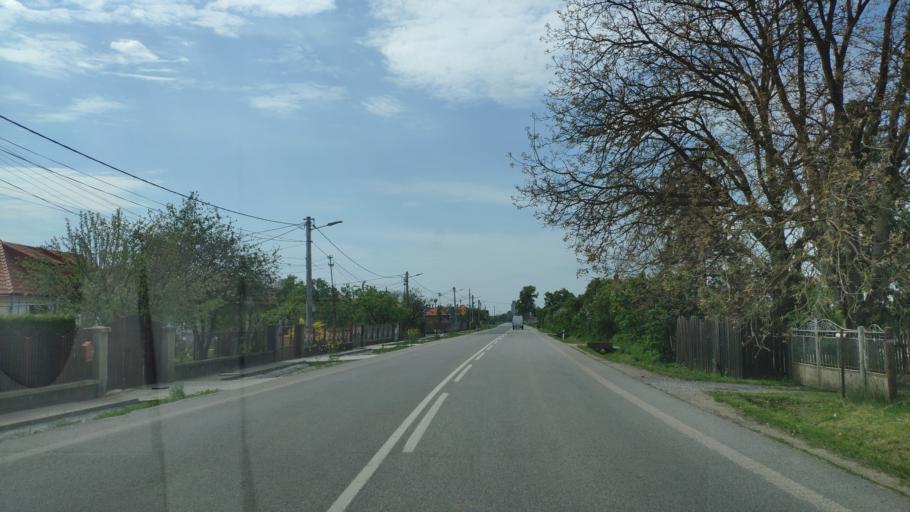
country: HU
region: Borsod-Abauj-Zemplen
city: Putnok
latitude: 48.4382
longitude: 20.3354
